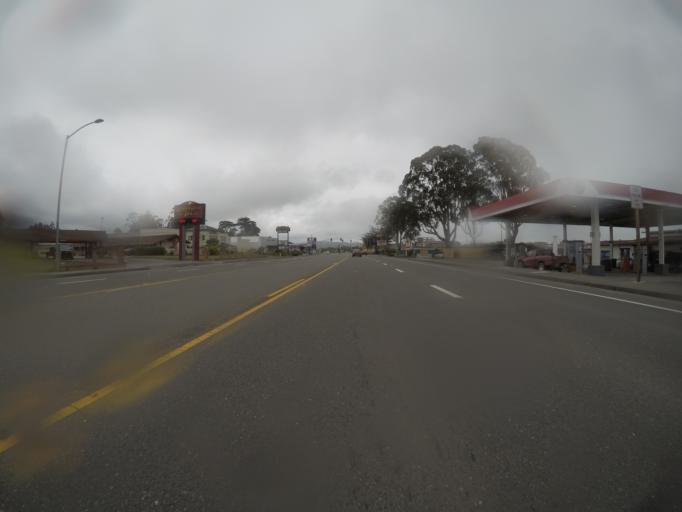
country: US
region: California
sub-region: Humboldt County
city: Bayview
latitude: 40.7700
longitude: -124.1915
